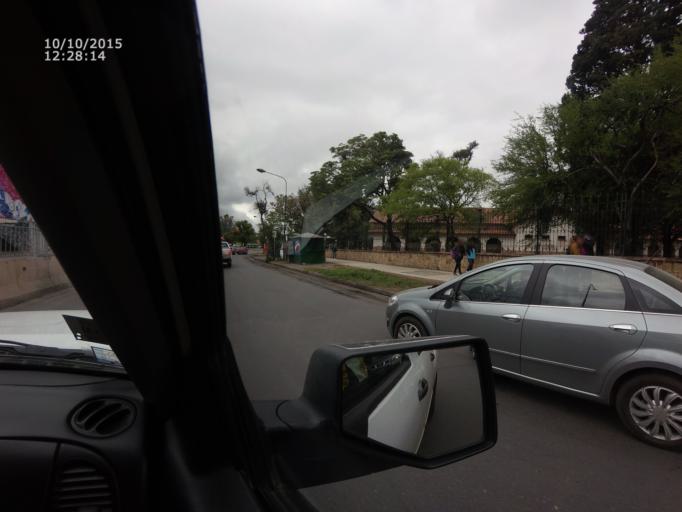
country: AR
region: Salta
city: Salta
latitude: -24.7958
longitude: -65.3989
